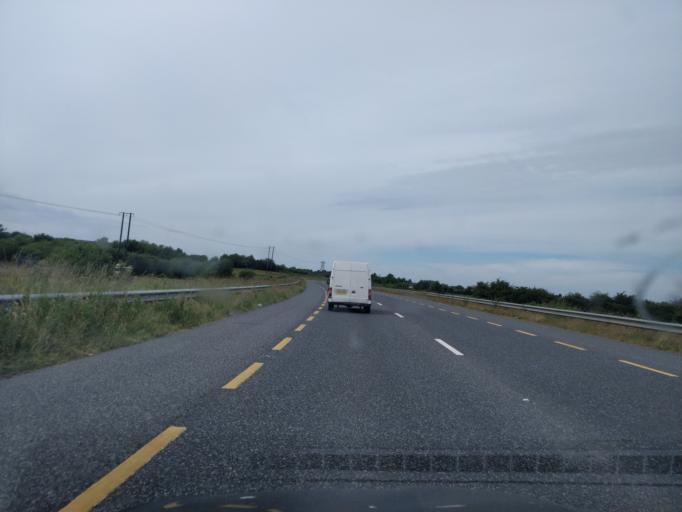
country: IE
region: Leinster
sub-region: Uibh Fhaili
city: Tullamore
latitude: 53.2710
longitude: -7.4639
